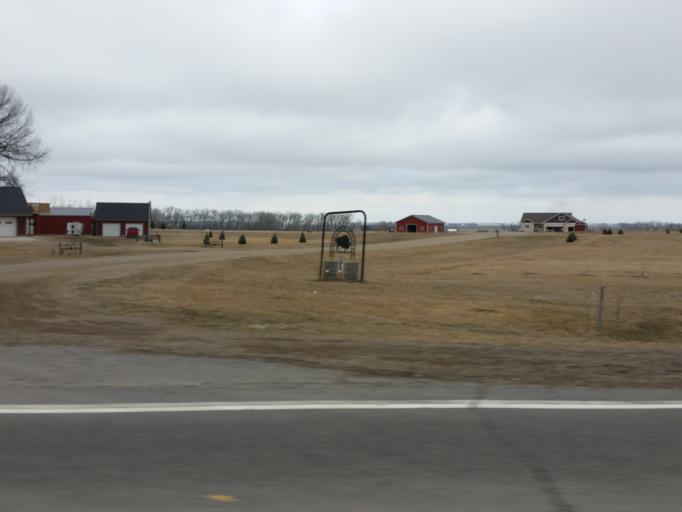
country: US
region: North Dakota
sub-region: Cass County
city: Horace
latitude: 46.6296
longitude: -97.1304
